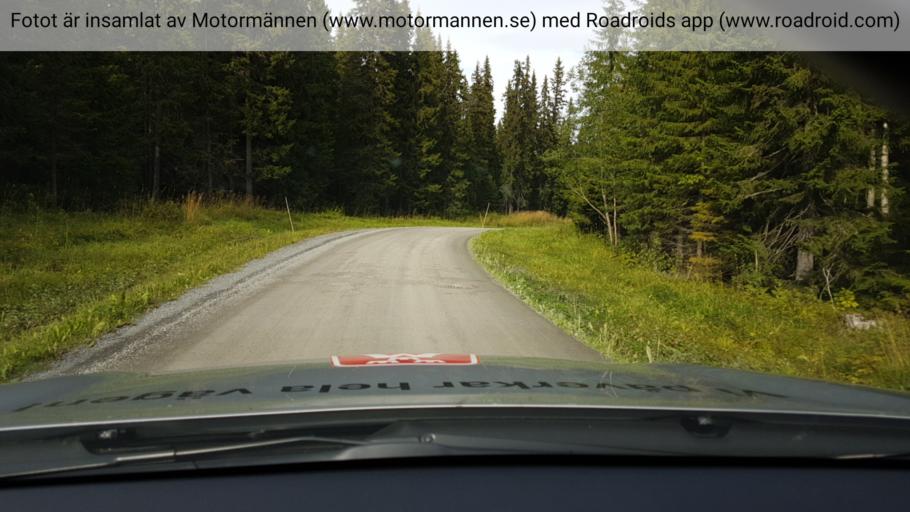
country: SE
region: Jaemtland
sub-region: Krokoms Kommun
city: Valla
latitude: 63.3908
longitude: 14.0616
